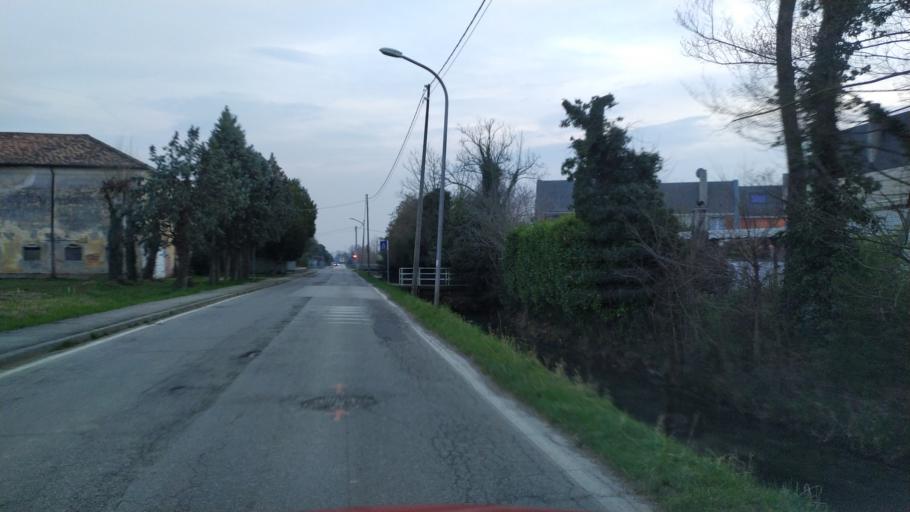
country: IT
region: Veneto
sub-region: Provincia di Vicenza
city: Vigardolo
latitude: 45.6084
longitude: 11.5870
